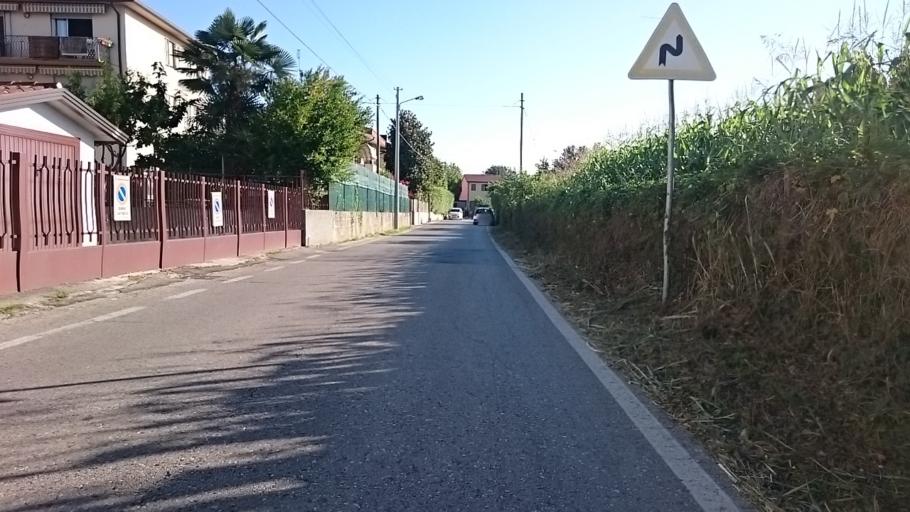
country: IT
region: Veneto
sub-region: Provincia di Padova
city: Mejaniga
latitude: 45.4395
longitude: 11.8971
